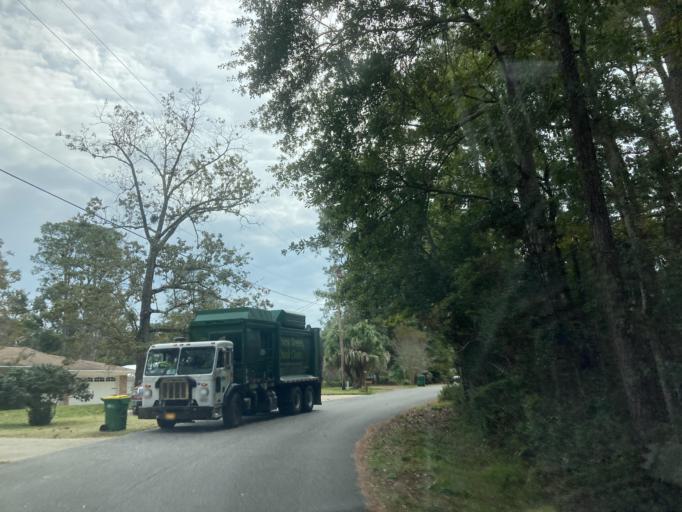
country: US
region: Mississippi
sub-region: Jackson County
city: Gulf Hills
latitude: 30.4338
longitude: -88.8420
